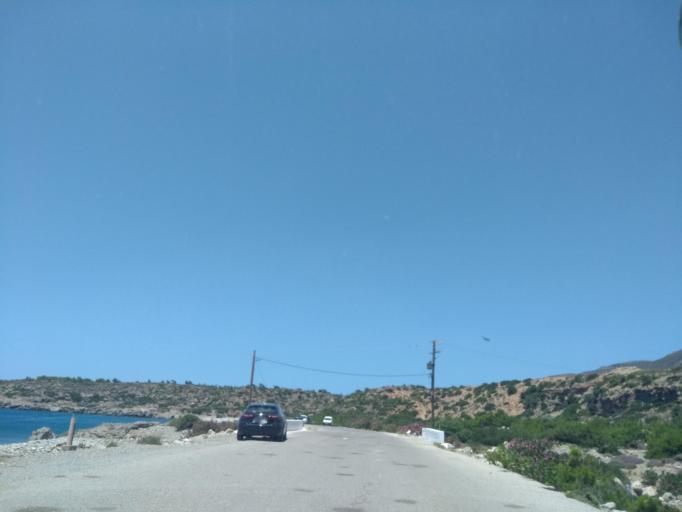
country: GR
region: Crete
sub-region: Nomos Chanias
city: Vryses
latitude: 35.3268
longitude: 23.5491
